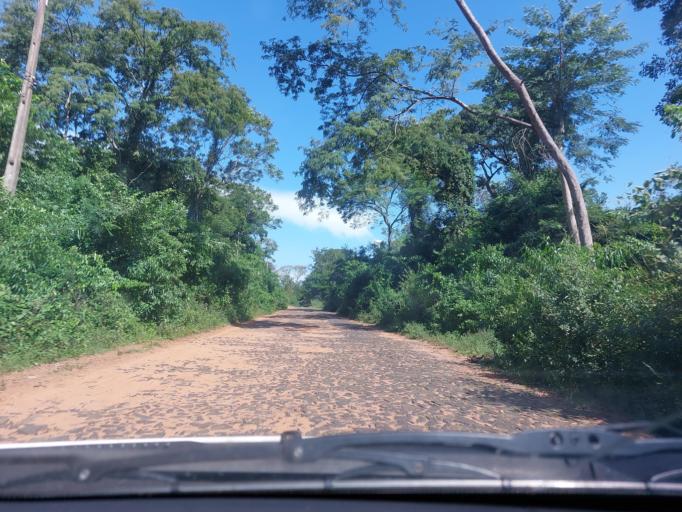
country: PY
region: San Pedro
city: Itacurubi del Rosario
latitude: -24.5784
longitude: -56.6003
